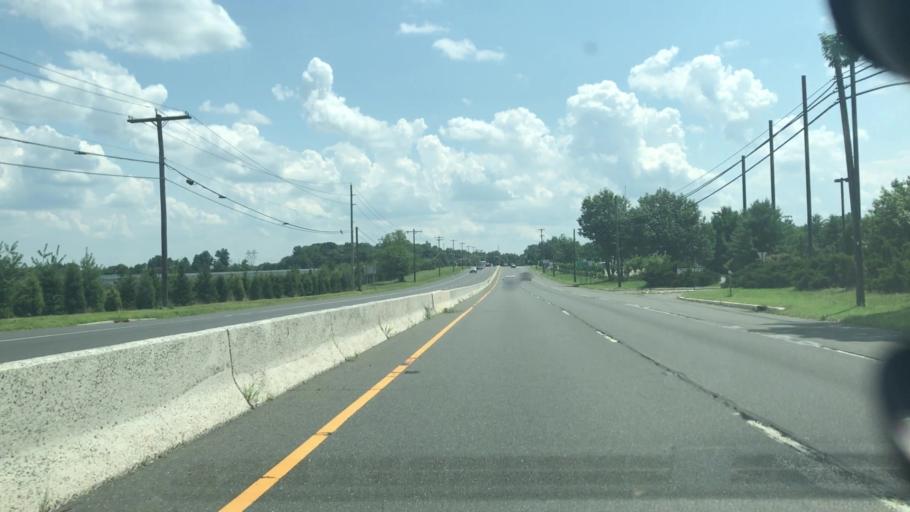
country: US
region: New Jersey
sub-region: Hunterdon County
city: Flemington
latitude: 40.4653
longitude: -74.8601
